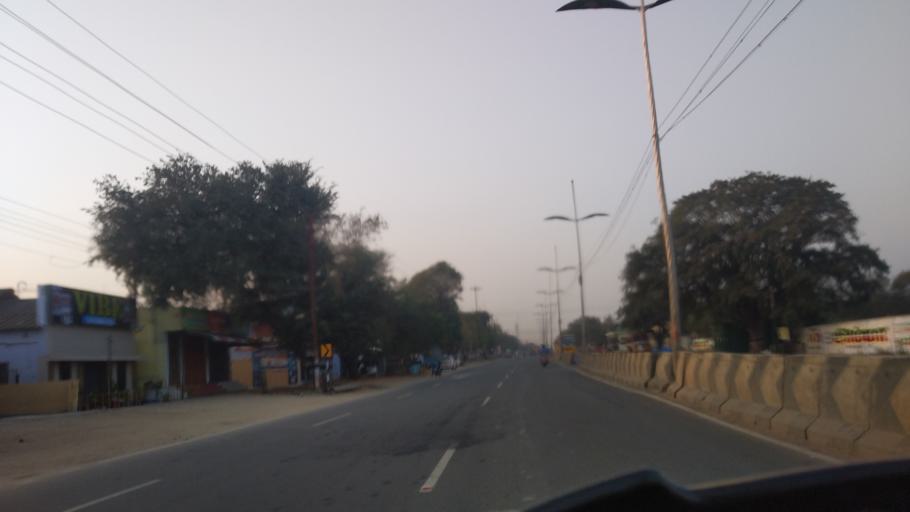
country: IN
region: Tamil Nadu
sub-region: Coimbatore
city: Madukkarai
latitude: 10.9489
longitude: 76.9535
